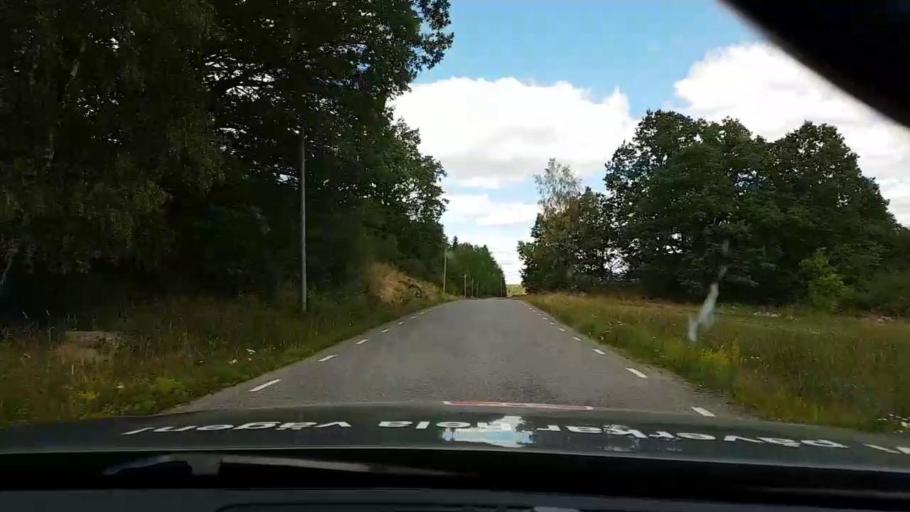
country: SE
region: Kalmar
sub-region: Vasterviks Kommun
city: Forserum
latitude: 57.9984
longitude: 16.5950
